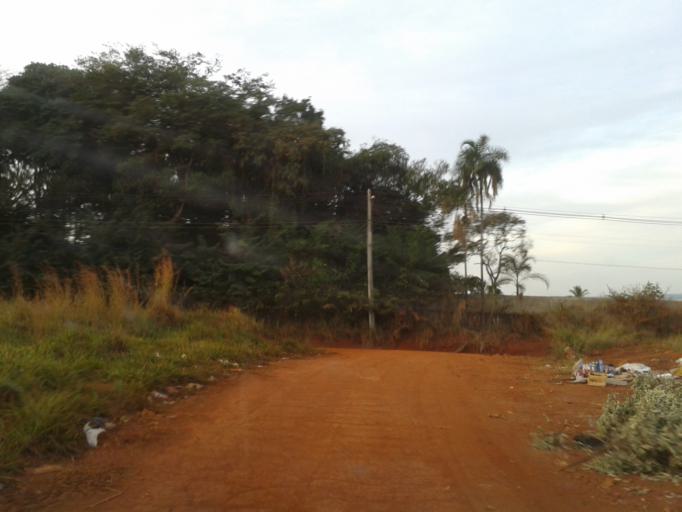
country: BR
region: Goias
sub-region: Goiania
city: Goiania
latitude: -16.6466
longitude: -49.3545
